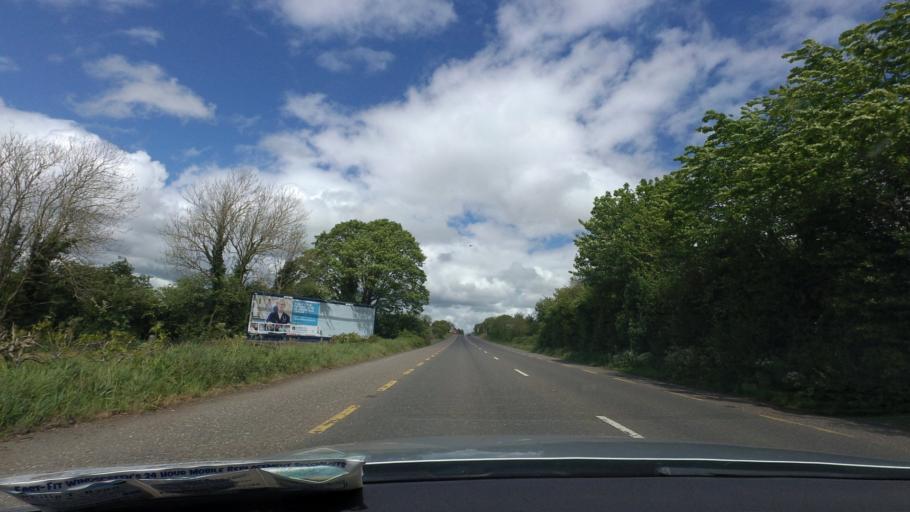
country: IE
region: Munster
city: Thurles
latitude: 52.6257
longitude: -7.7612
